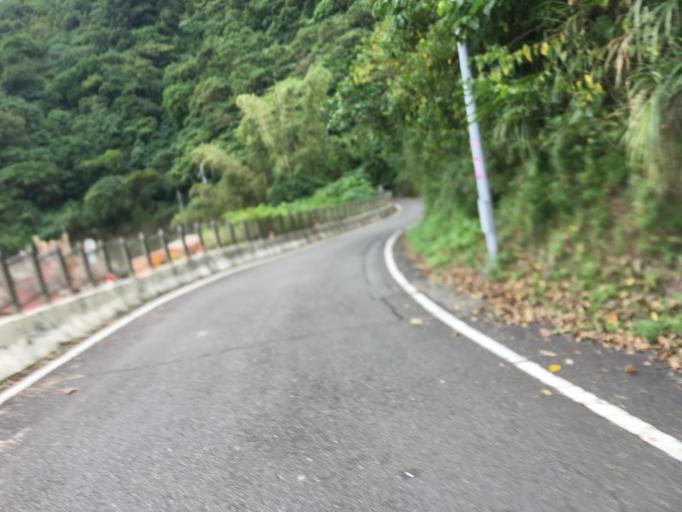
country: TW
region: Taiwan
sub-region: Yilan
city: Yilan
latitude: 24.5784
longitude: 121.8681
